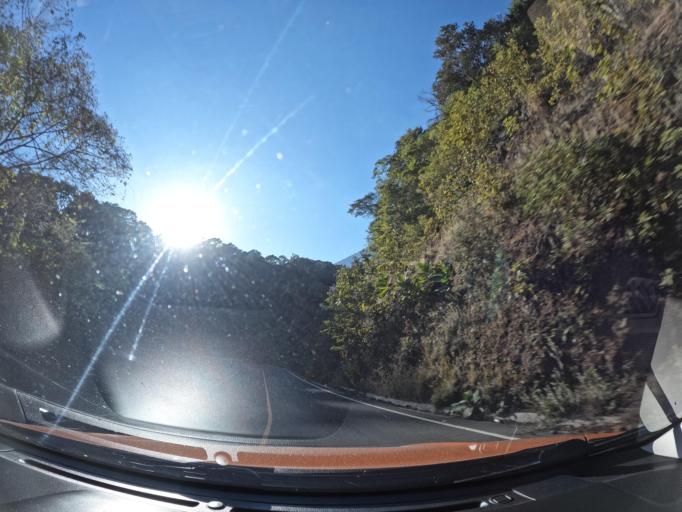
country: GT
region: Escuintla
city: Palin
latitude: 14.4588
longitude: -90.6958
